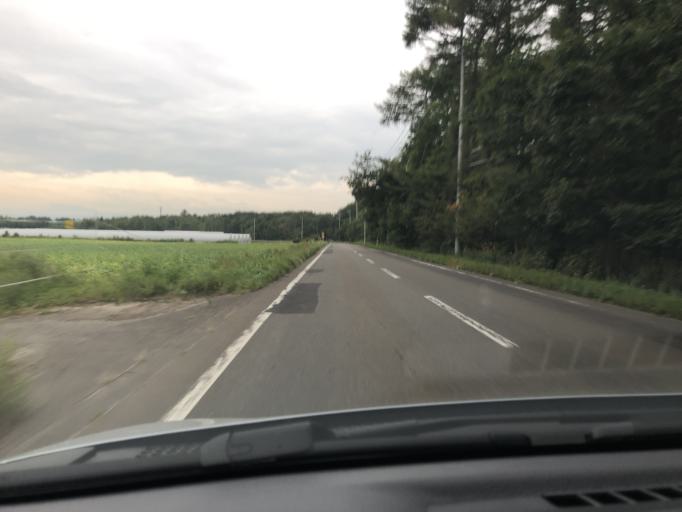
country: JP
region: Hokkaido
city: Chitose
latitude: 42.8718
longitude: 141.7239
